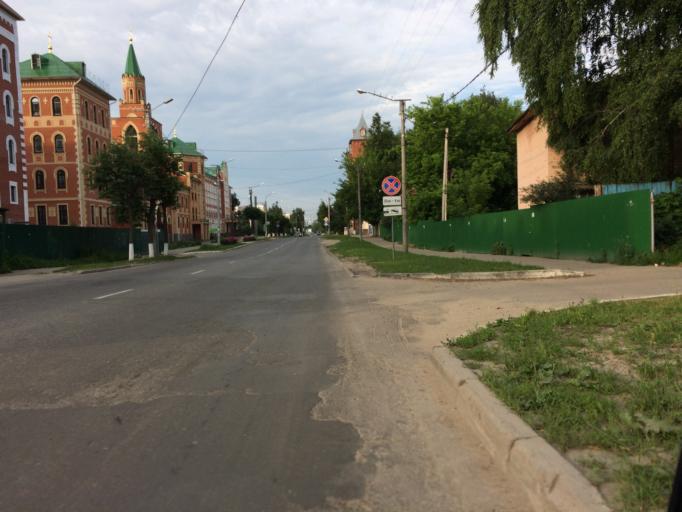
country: RU
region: Mariy-El
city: Yoshkar-Ola
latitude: 56.6330
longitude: 47.8986
